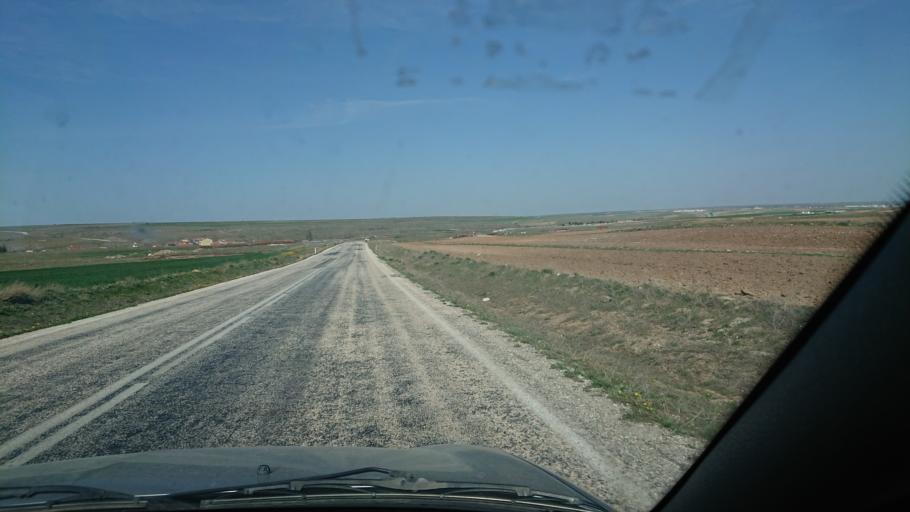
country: TR
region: Eskisehir
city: Eskisehir
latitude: 39.6715
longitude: 30.4765
